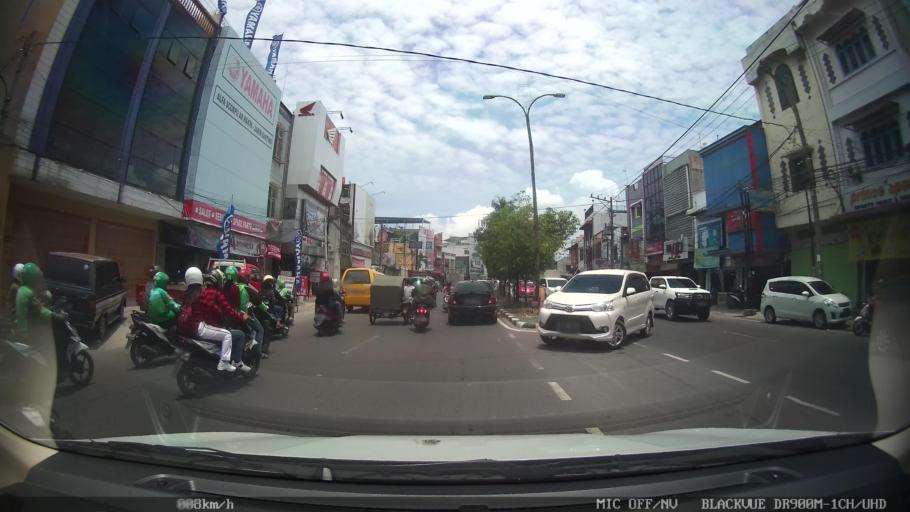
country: ID
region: North Sumatra
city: Medan
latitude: 3.5699
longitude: 98.6600
